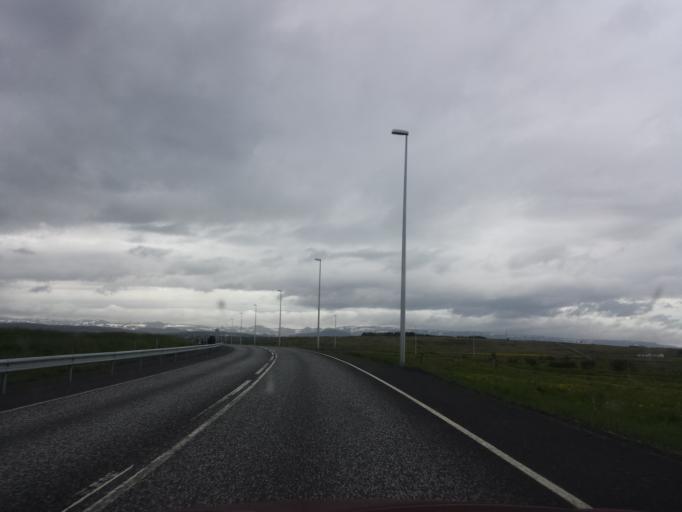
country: IS
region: Capital Region
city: Alftanes
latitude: 64.0977
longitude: -22.0048
